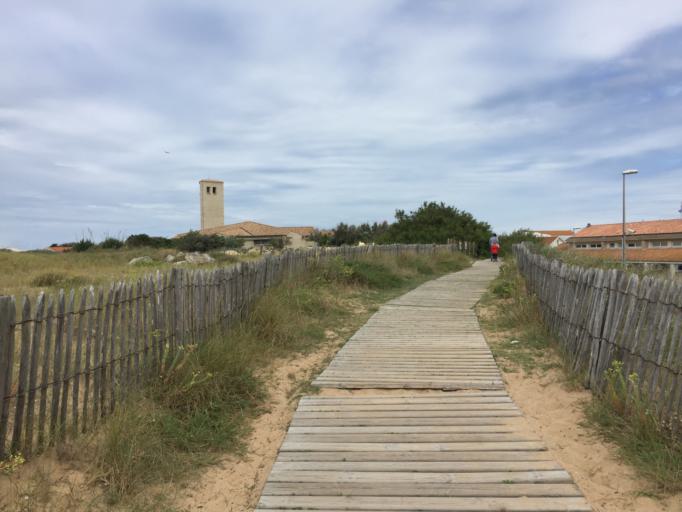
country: FR
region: Poitou-Charentes
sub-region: Departement de la Charente-Maritime
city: Dolus-d'Oleron
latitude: 45.9141
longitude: -1.3301
